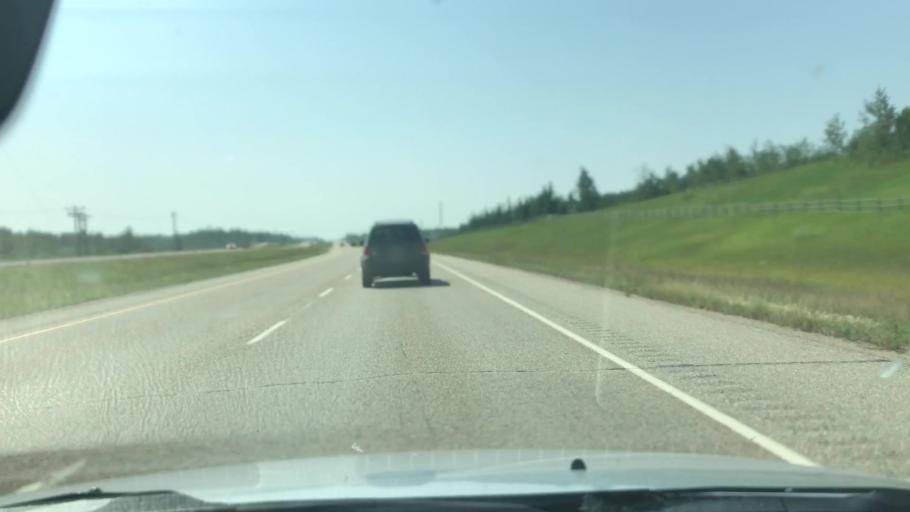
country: CA
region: Alberta
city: Devon
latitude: 53.4494
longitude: -113.7625
